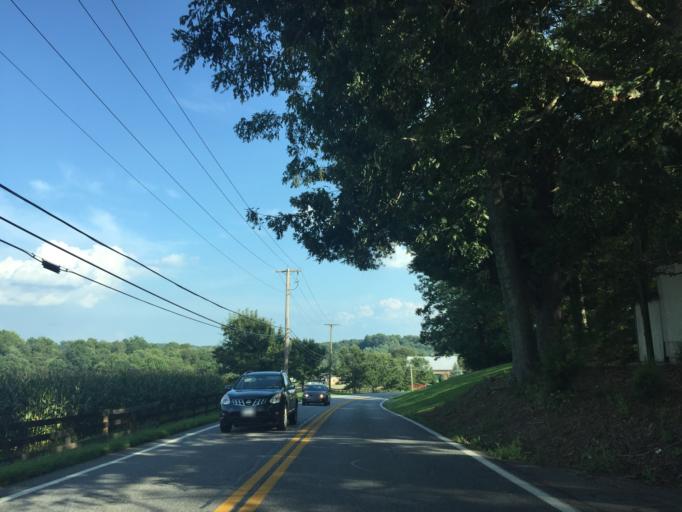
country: US
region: Maryland
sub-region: Carroll County
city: Hampstead
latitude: 39.6234
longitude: -76.7937
